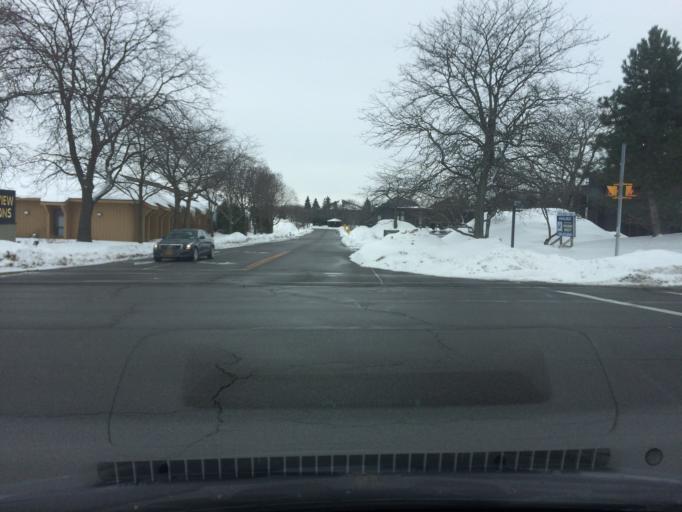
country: US
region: New York
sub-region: Monroe County
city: Rochester
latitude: 43.1061
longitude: -77.6189
